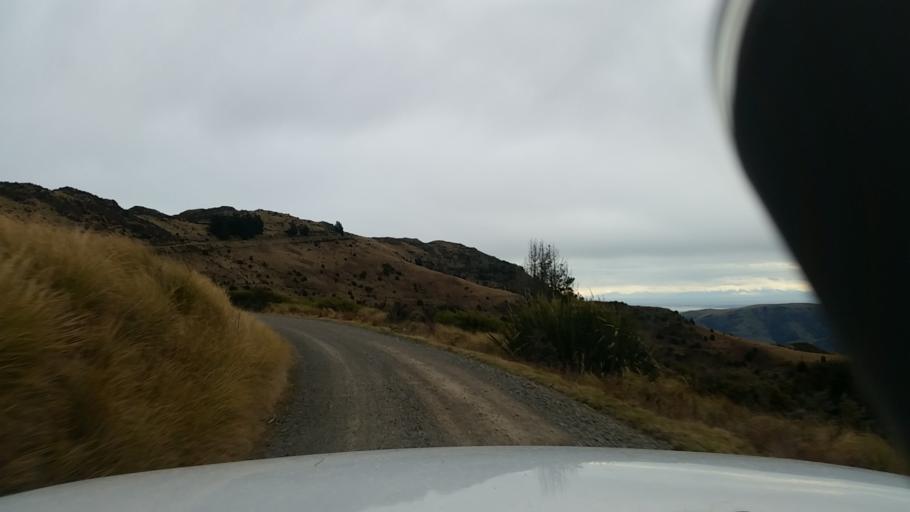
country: NZ
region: Canterbury
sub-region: Christchurch City
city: Christchurch
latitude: -43.8085
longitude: 172.8421
